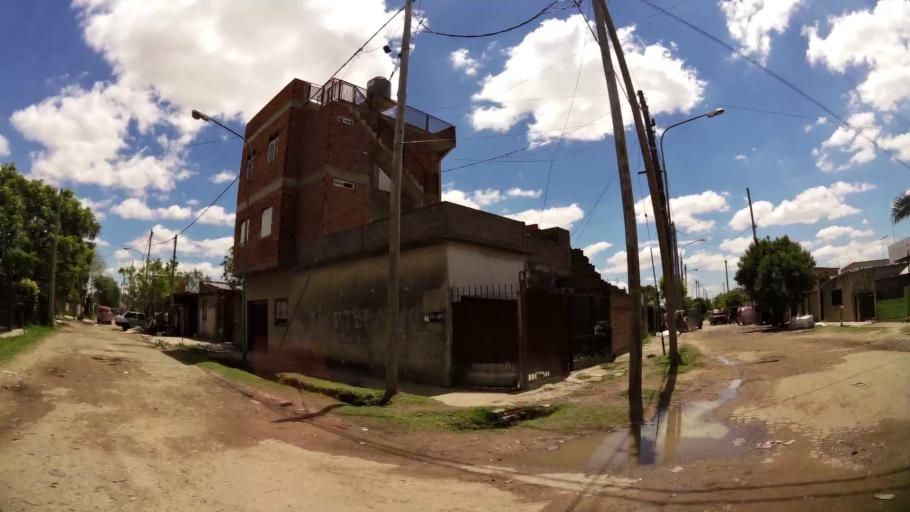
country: AR
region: Buenos Aires
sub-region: Partido de Lanus
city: Lanus
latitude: -34.7197
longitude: -58.4216
